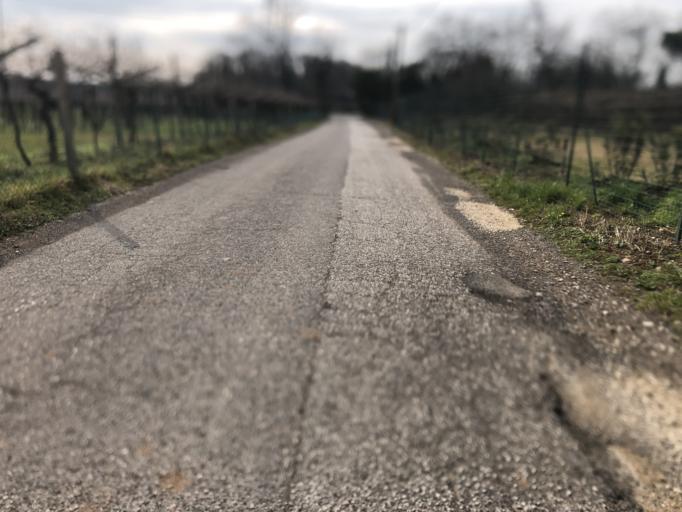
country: IT
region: Veneto
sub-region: Provincia di Verona
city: Sona
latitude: 45.4194
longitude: 10.8192
